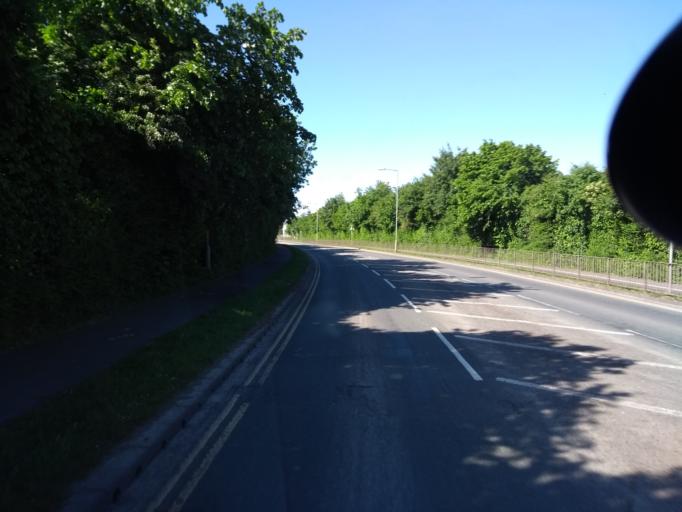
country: GB
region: England
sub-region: Somerset
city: Bridgwater
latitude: 51.1383
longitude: -3.0113
